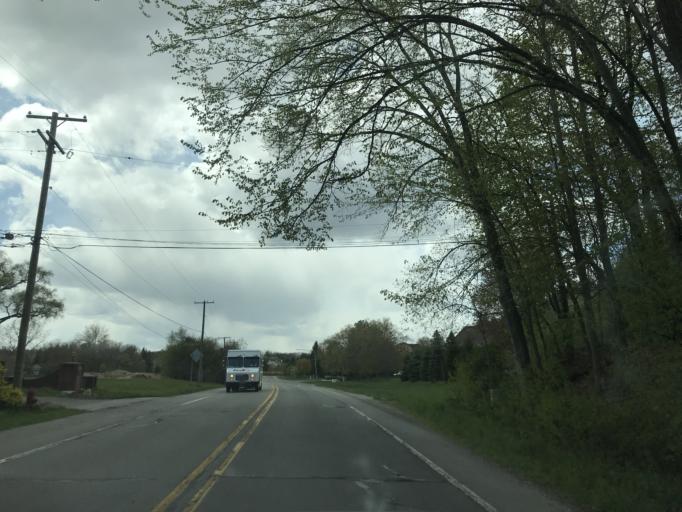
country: US
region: Michigan
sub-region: Wayne County
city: Plymouth
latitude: 42.3770
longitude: -83.4906
